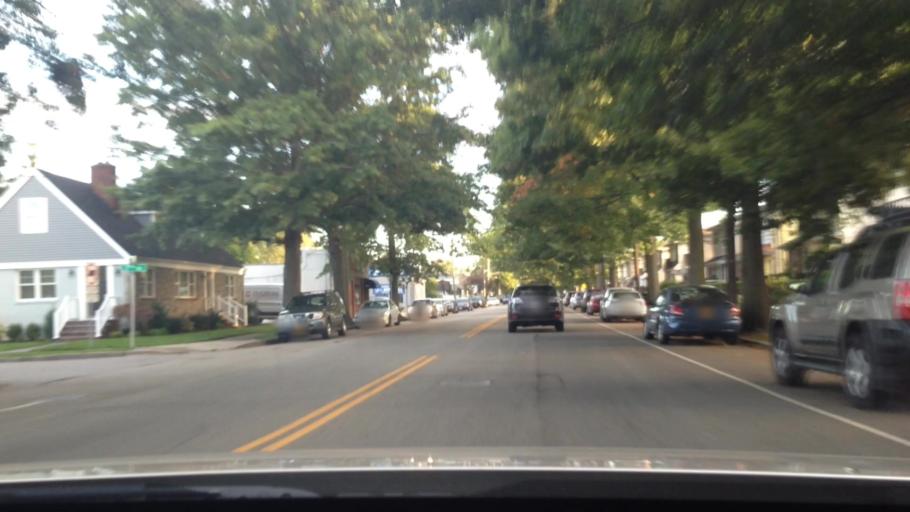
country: US
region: New York
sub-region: Nassau County
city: Garden City South
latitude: 40.7105
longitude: -73.6610
